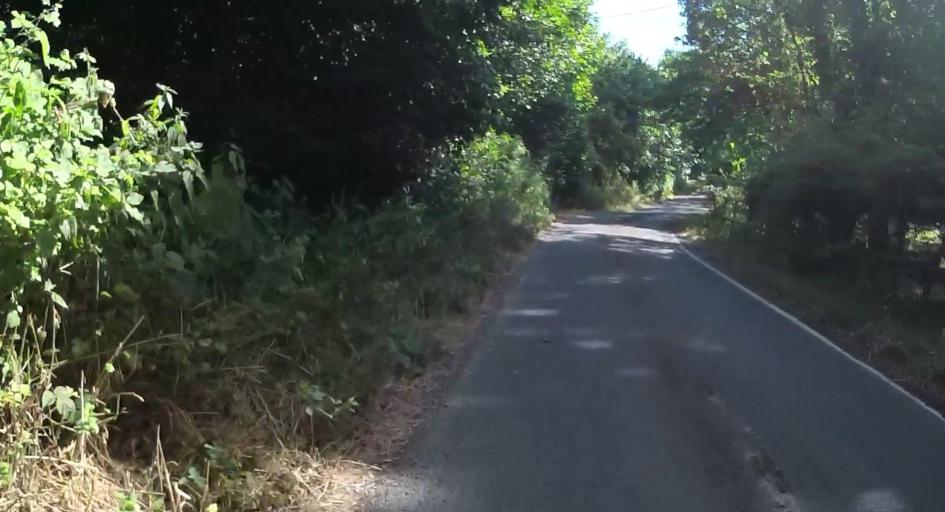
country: GB
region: England
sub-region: Dorset
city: Wool
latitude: 50.7146
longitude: -2.1921
